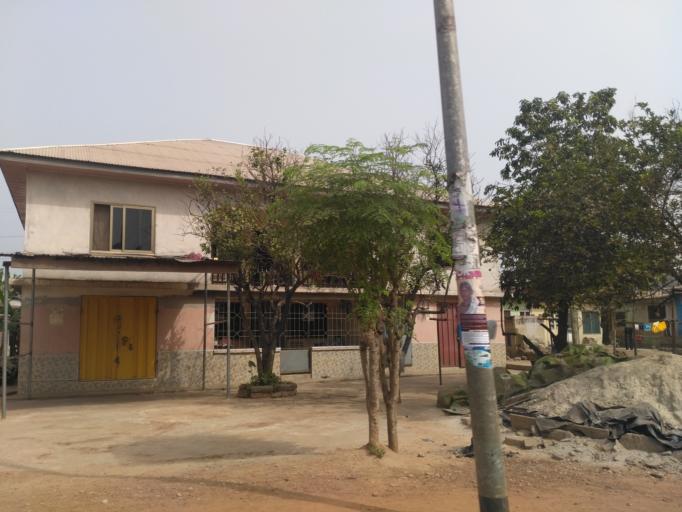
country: GH
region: Ashanti
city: Kumasi
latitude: 6.6696
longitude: -1.6316
